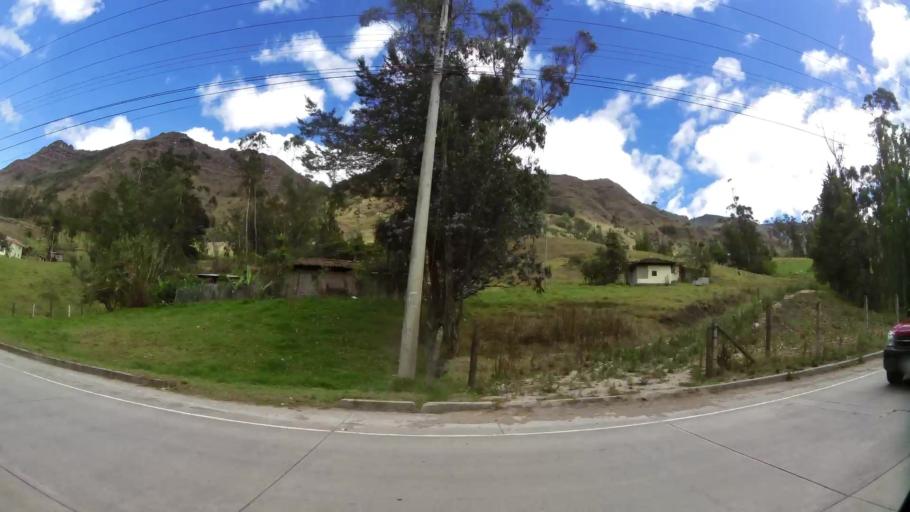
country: EC
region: Azuay
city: Cuenca
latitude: -3.1397
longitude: -79.1387
